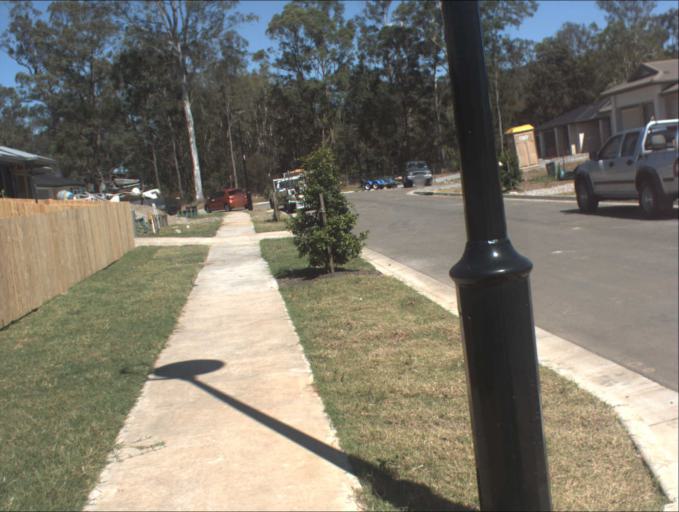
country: AU
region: Queensland
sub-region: Logan
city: Windaroo
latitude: -27.7561
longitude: 153.1885
